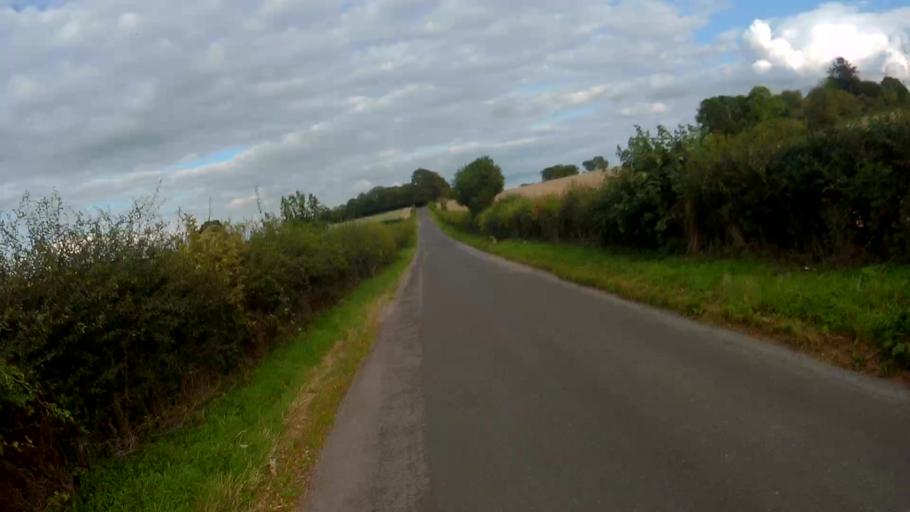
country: GB
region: England
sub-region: Hampshire
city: Kings Worthy
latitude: 51.1340
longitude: -1.2046
